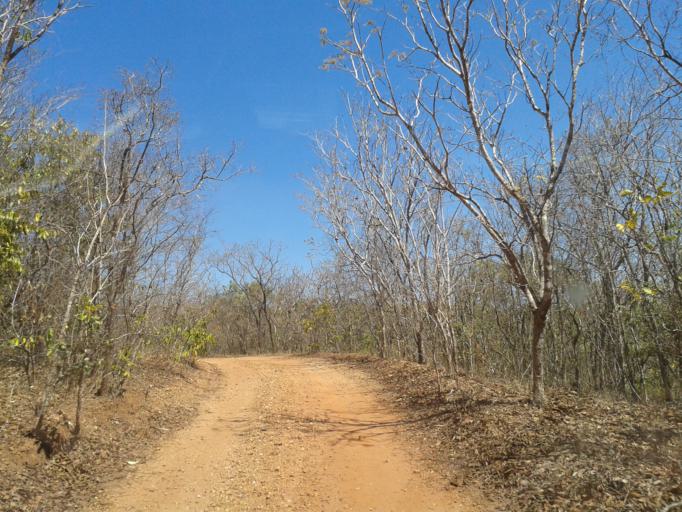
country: BR
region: Minas Gerais
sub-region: Ituiutaba
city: Ituiutaba
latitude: -19.1213
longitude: -49.2984
